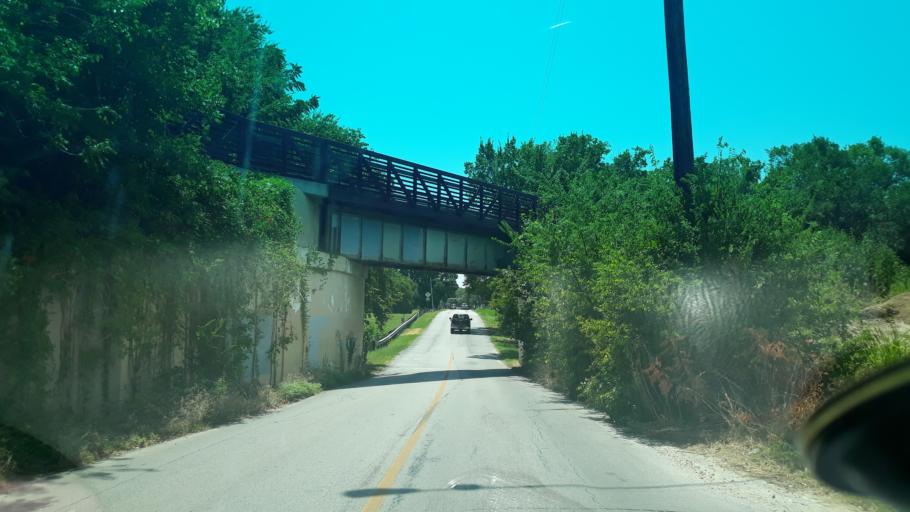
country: US
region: Texas
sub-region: Dallas County
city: Highland Park
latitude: 32.8153
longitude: -96.7298
